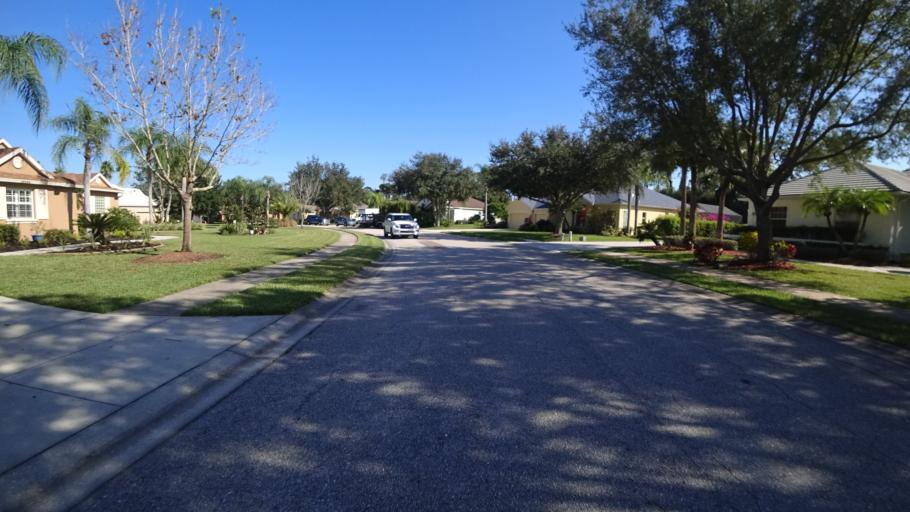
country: US
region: Florida
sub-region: Sarasota County
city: The Meadows
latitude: 27.4041
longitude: -82.4386
